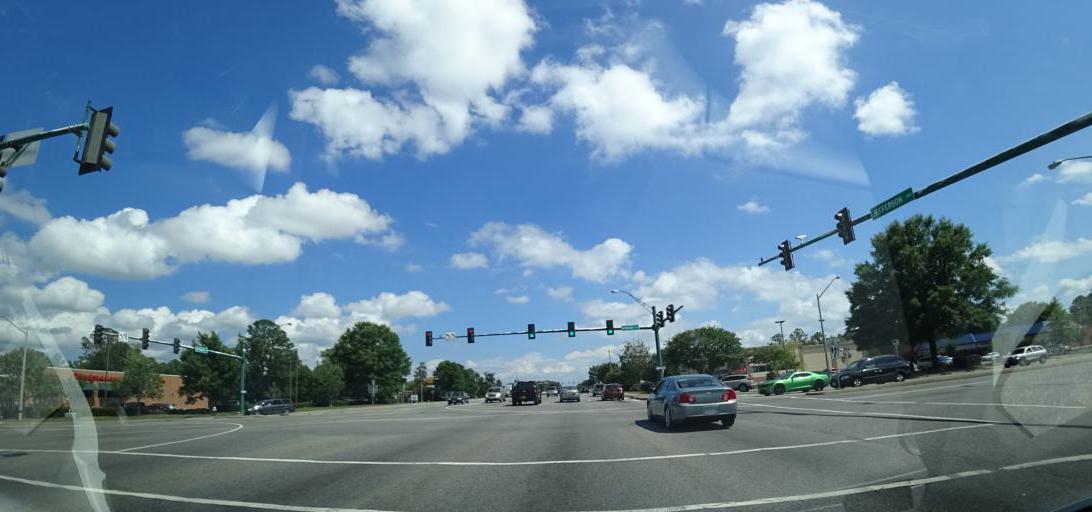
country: US
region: Virginia
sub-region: York County
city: Yorktown
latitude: 37.1388
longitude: -76.5203
